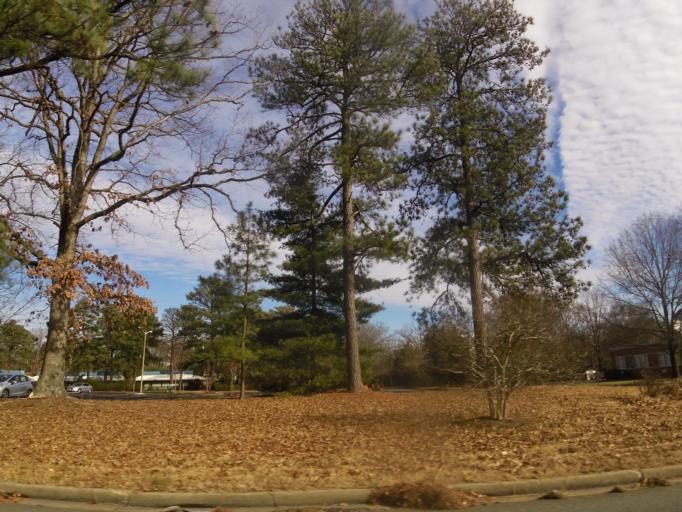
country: US
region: Virginia
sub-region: Henrico County
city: Dumbarton
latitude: 37.5827
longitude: -77.5082
